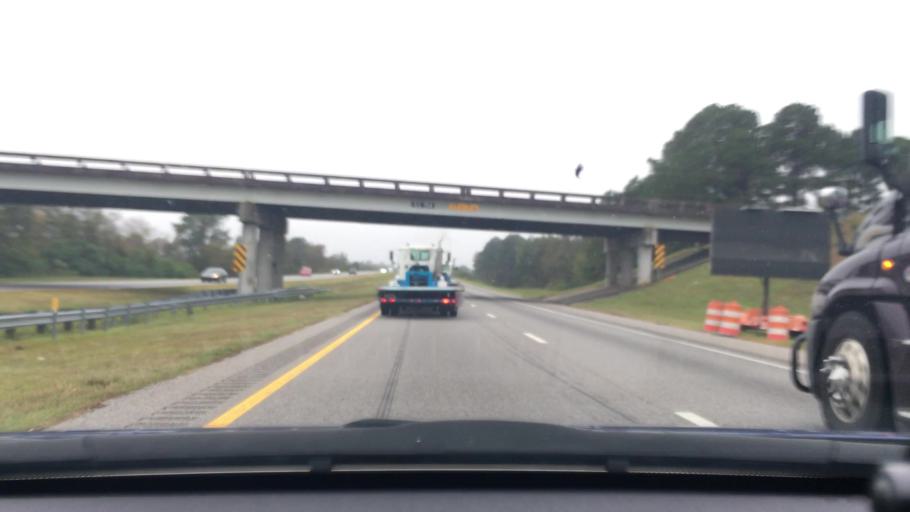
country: US
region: South Carolina
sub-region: Lee County
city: Bishopville
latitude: 34.1902
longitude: -80.2499
